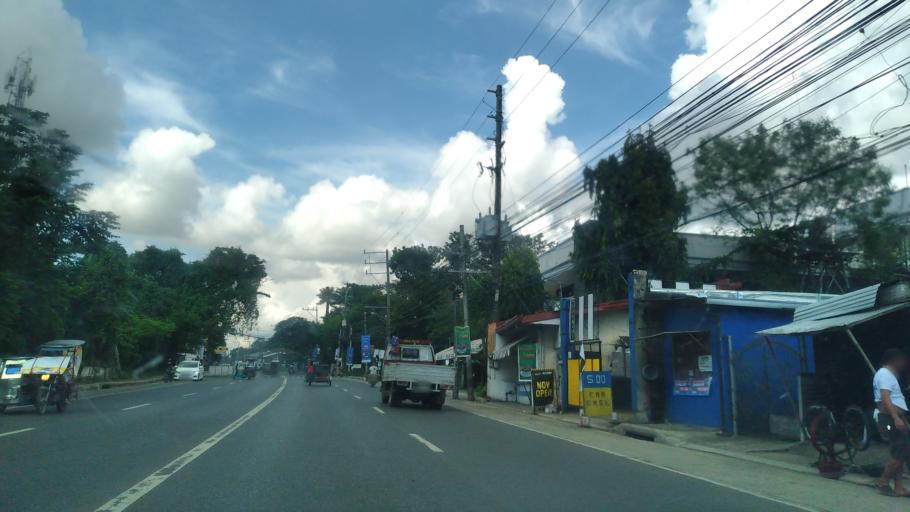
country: PH
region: Calabarzon
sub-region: Province of Quezon
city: Isabang
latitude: 13.9459
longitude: 121.5901
